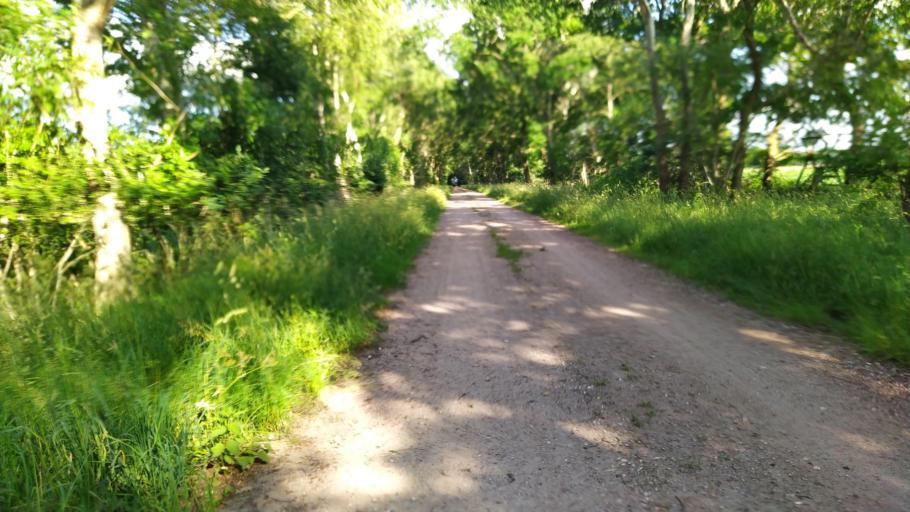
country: DE
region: Lower Saxony
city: Lintig
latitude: 53.6169
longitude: 8.8808
